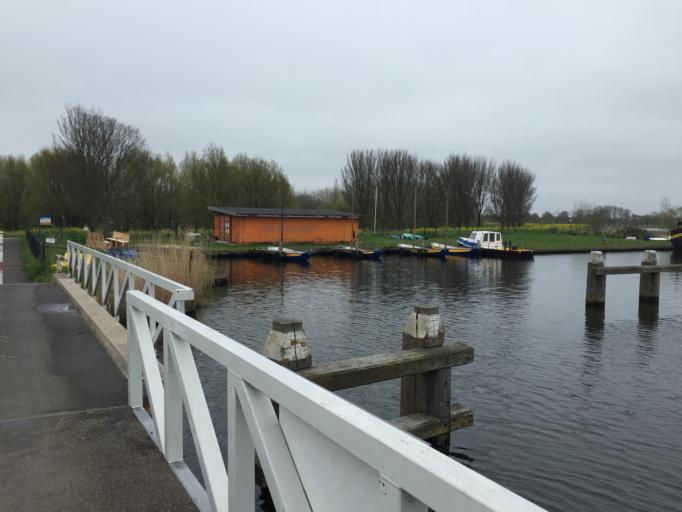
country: NL
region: North Holland
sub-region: Gemeente Velsen
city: Velsen-Zuid
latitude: 52.4187
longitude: 4.6818
